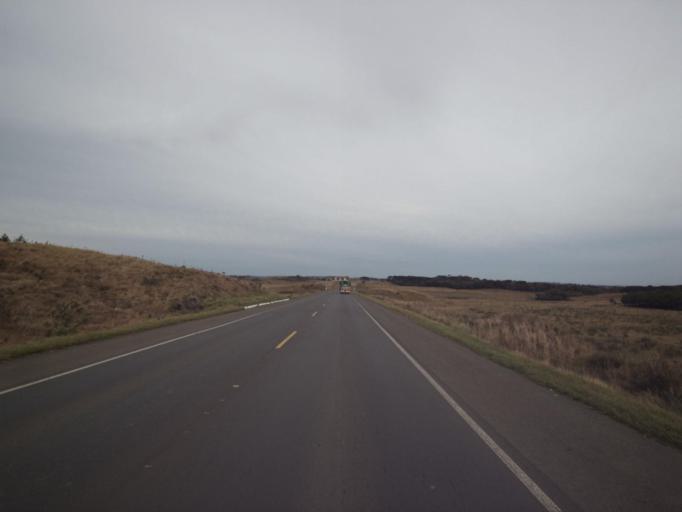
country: BR
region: Santa Catarina
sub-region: Cacador
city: Cacador
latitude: -26.6165
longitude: -51.4984
